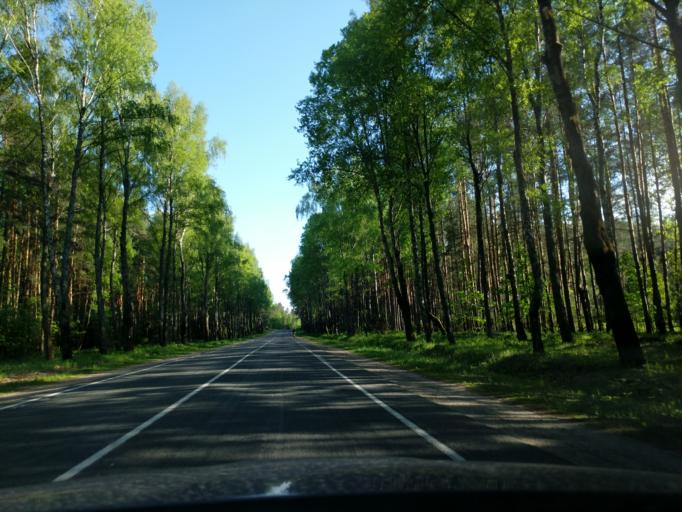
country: BY
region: Minsk
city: Myadzyel
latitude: 54.8489
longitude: 26.9257
